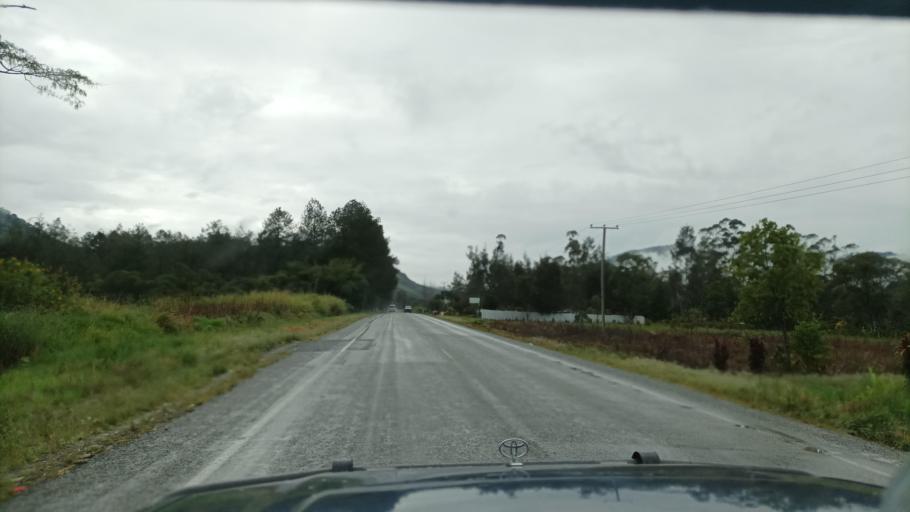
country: PG
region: Western Highlands
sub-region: Hagen
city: Mount Hagen
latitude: -5.8364
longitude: 144.3341
